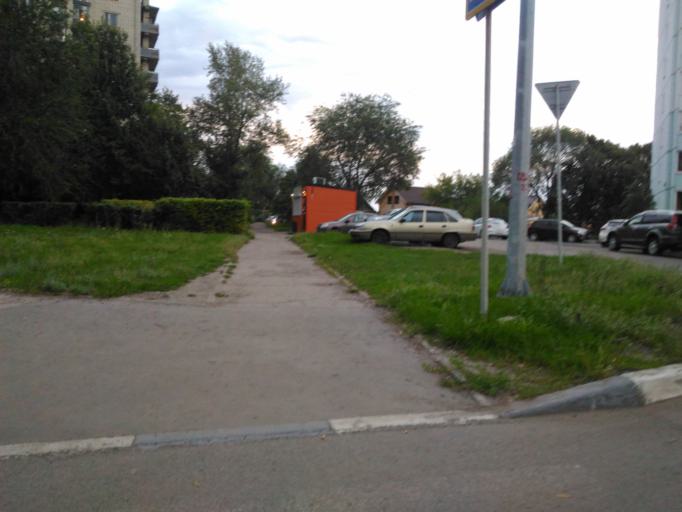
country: RU
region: Ulyanovsk
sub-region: Ulyanovskiy Rayon
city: Ulyanovsk
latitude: 54.2774
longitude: 48.3435
